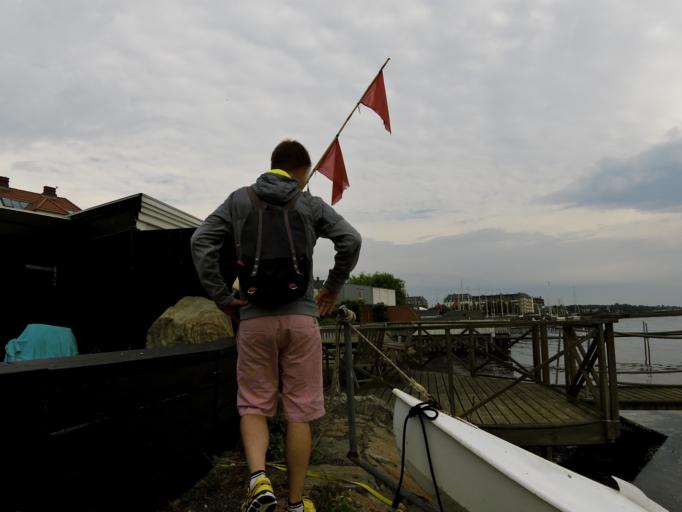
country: DK
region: Capital Region
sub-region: Gentofte Kommune
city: Charlottenlund
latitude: 55.7293
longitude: 12.5818
